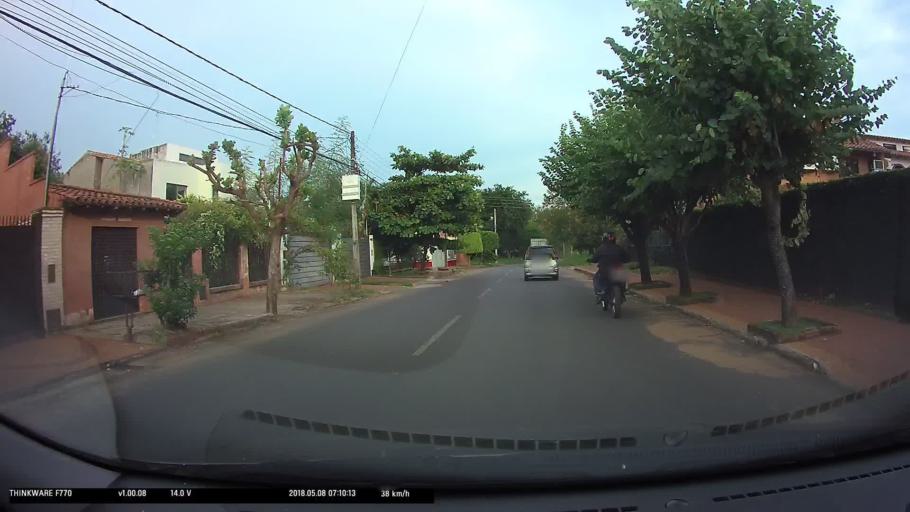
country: PY
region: Central
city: Fernando de la Mora
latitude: -25.2601
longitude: -57.5087
